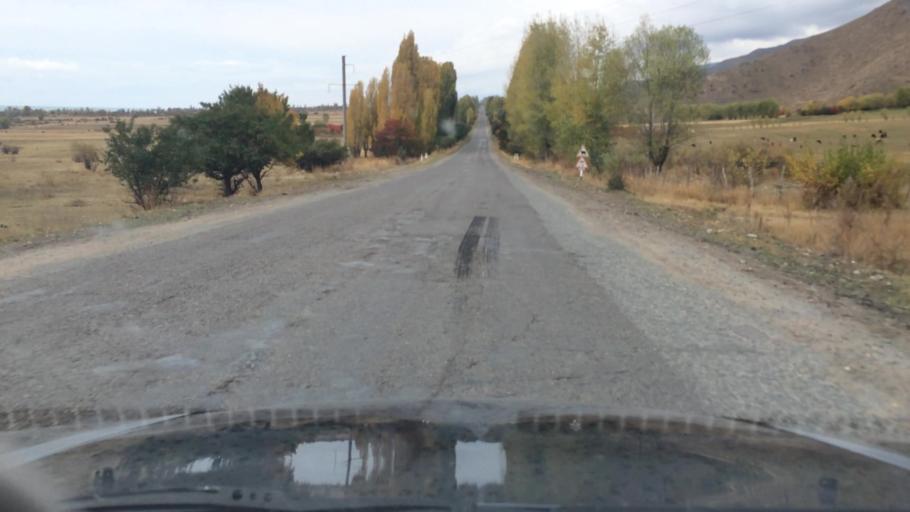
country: KG
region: Ysyk-Koel
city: Pokrovka
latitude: 42.7357
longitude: 77.9689
